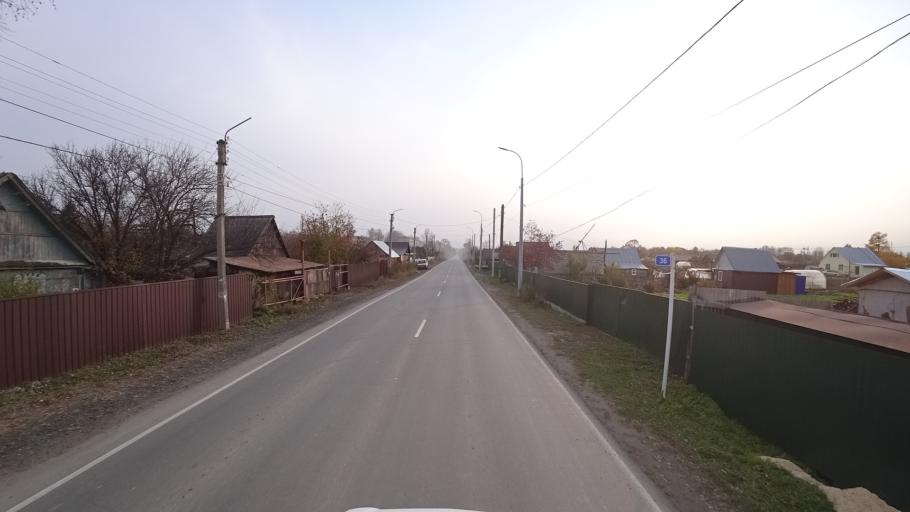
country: RU
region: Khabarovsk Krai
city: Amursk
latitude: 50.1033
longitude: 136.5116
